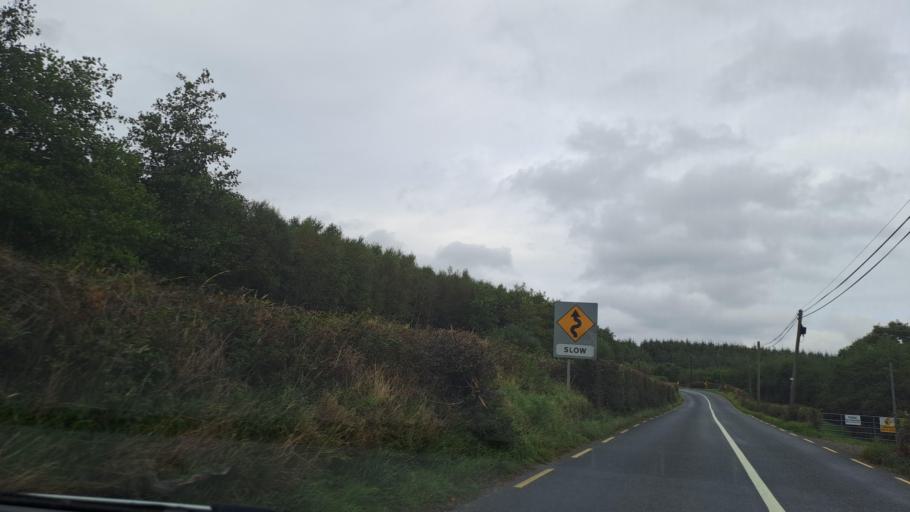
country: IE
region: Ulster
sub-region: An Cabhan
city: Bailieborough
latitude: 53.9305
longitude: -6.9667
